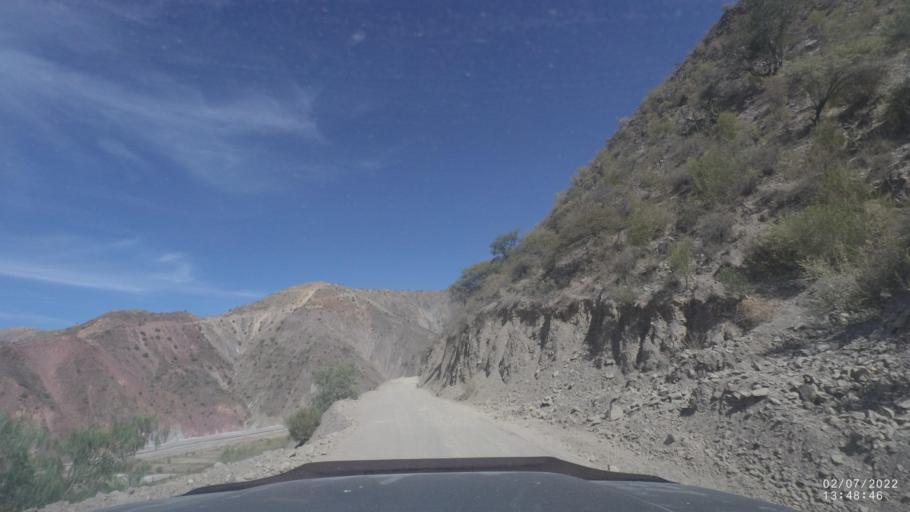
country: BO
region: Cochabamba
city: Irpa Irpa
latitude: -17.8178
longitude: -66.3739
